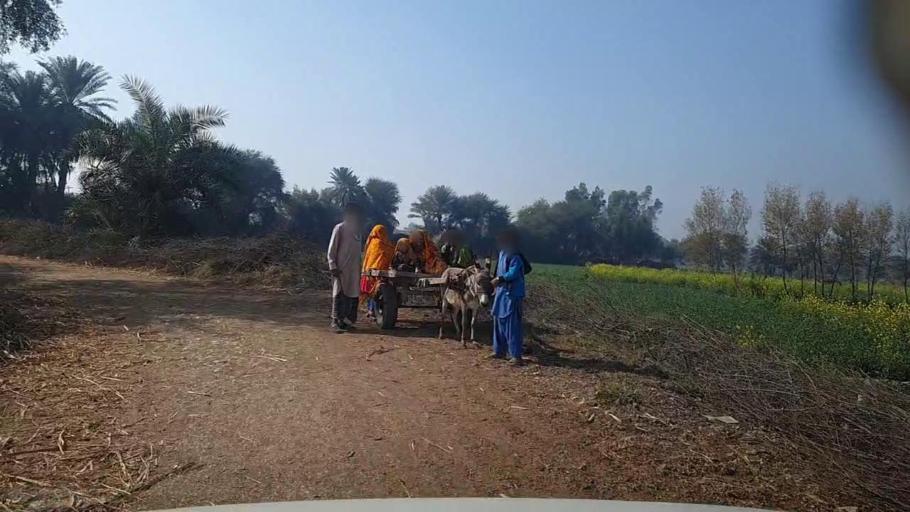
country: PK
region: Sindh
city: Khairpur
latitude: 27.9415
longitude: 69.6589
